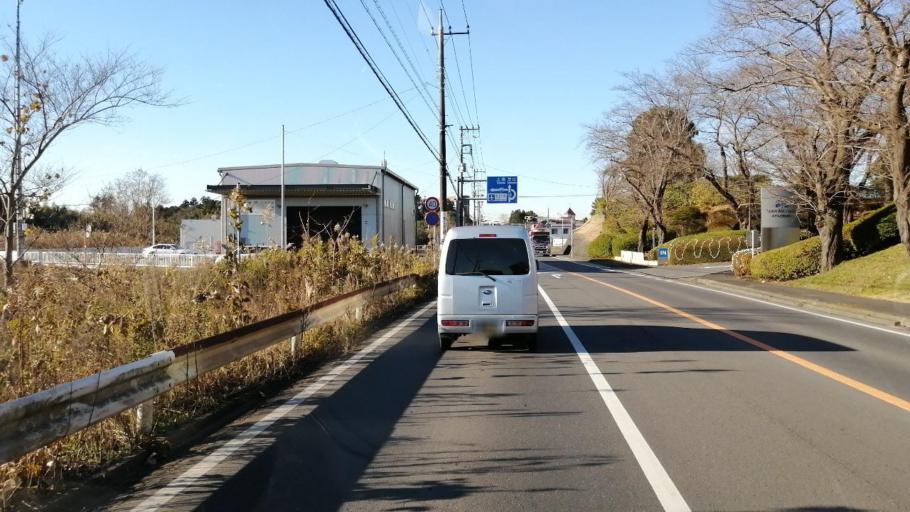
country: JP
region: Chiba
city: Narita
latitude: 35.7833
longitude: 140.3802
